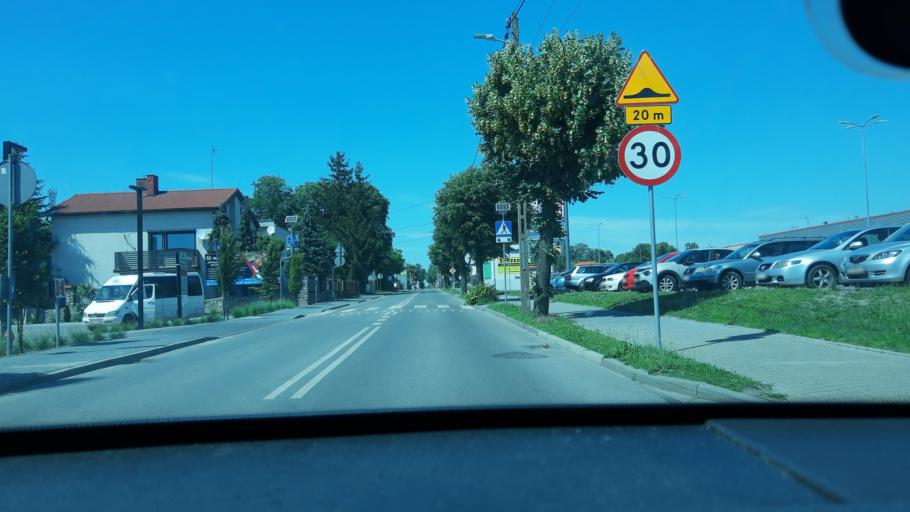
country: PL
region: Lodz Voivodeship
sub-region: Powiat zdunskowolski
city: Zdunska Wola
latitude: 51.6082
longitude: 18.9387
